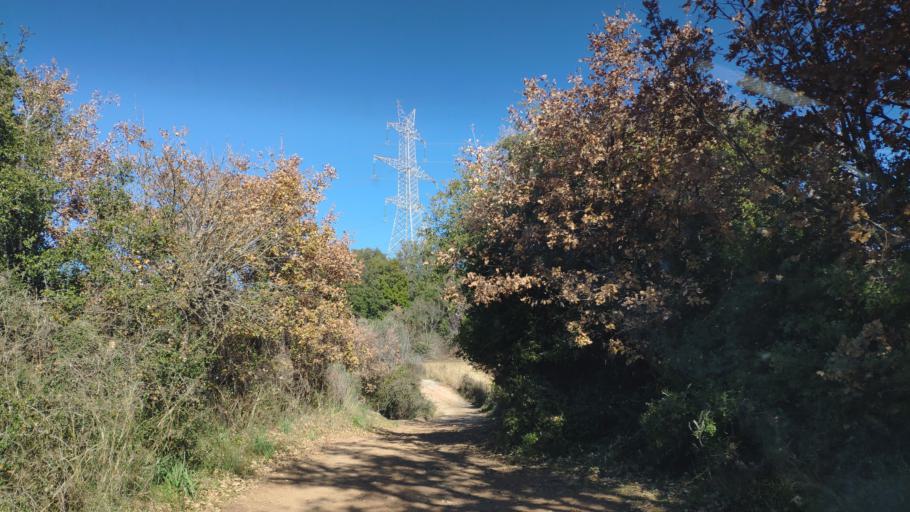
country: GR
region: West Greece
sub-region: Nomos Aitolias kai Akarnanias
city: Thermo
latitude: 38.5813
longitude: 21.6308
